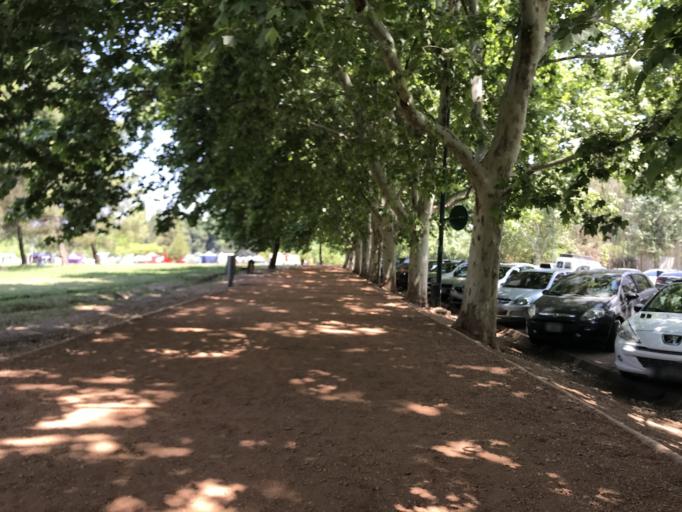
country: AR
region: Mendoza
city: Mendoza
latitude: -32.8957
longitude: -68.8673
